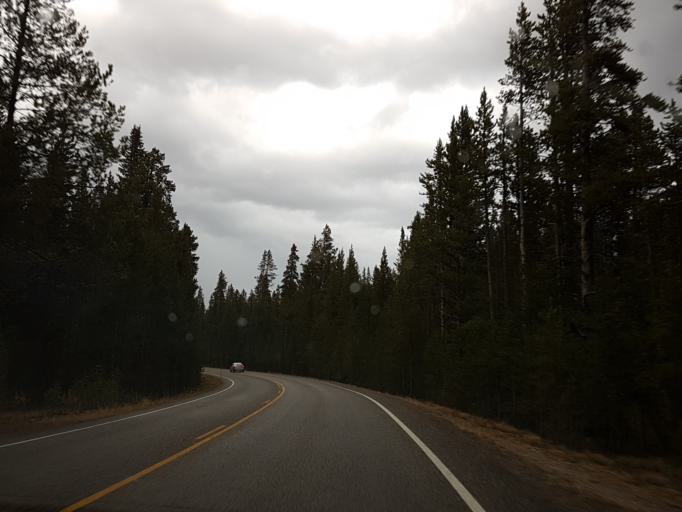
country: US
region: Montana
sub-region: Gallatin County
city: West Yellowstone
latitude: 44.4592
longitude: -110.5092
